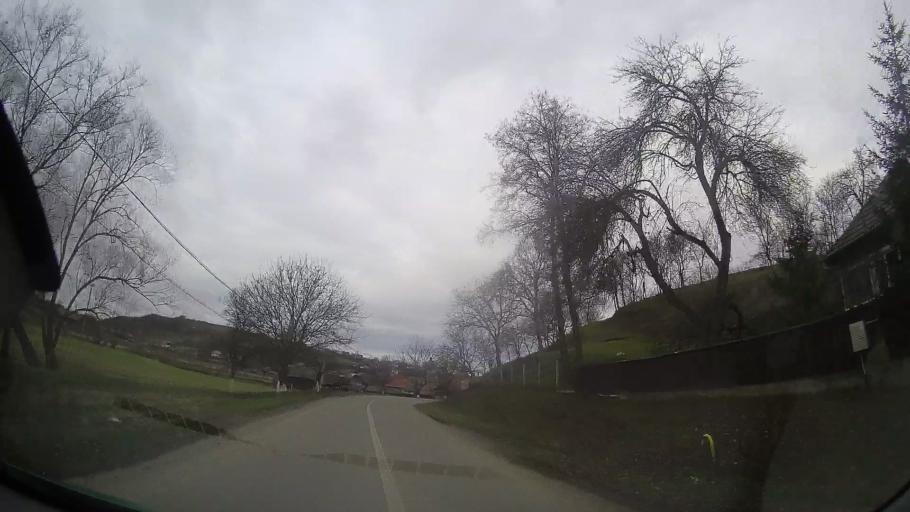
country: RO
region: Mures
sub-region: Comuna Faragau
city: Faragau
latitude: 46.7576
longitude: 24.5179
